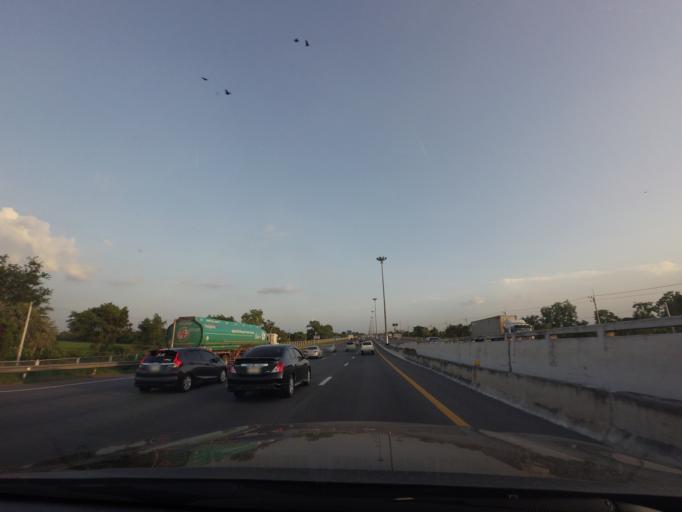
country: TH
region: Pathum Thani
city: Khlong Luang
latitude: 14.1201
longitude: 100.6758
